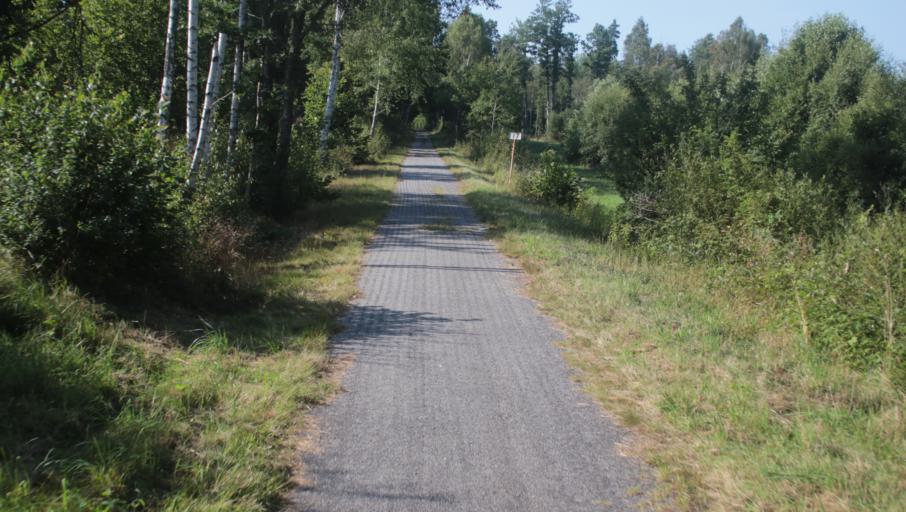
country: SE
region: Blekinge
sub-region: Karlshamns Kommun
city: Svangsta
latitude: 56.3034
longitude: 14.7289
